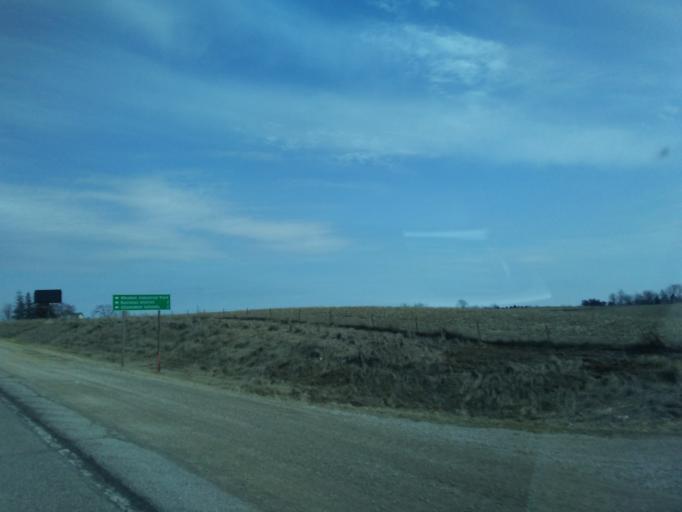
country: US
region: Iowa
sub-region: Allamakee County
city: Waukon
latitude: 43.2404
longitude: -91.4931
